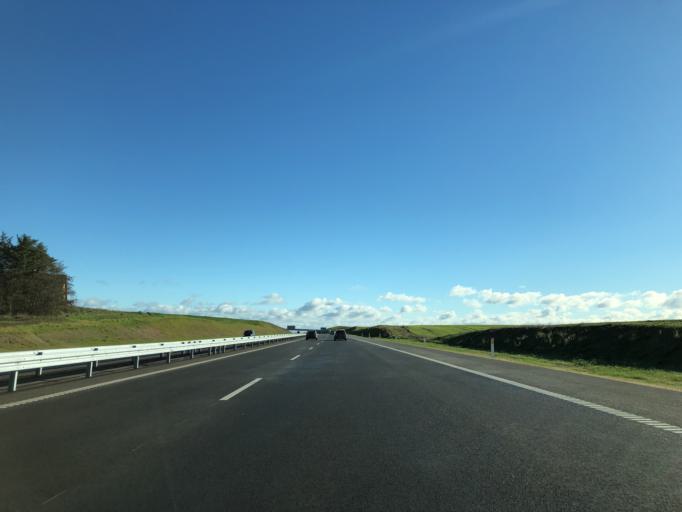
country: DK
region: Central Jutland
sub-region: Holstebro Kommune
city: Holstebro
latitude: 56.3836
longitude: 8.6625
